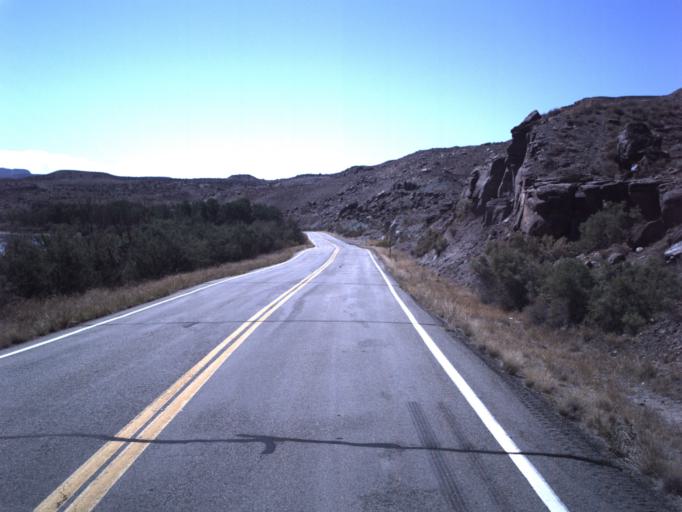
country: US
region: Utah
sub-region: Grand County
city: Moab
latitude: 38.8398
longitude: -109.2853
